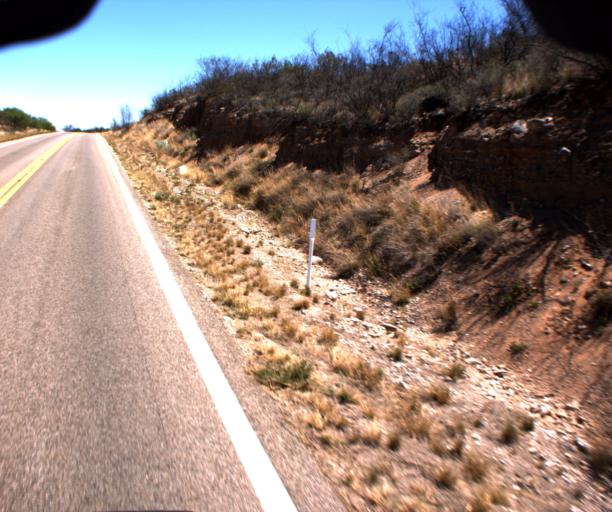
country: US
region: Arizona
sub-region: Cochise County
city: Tombstone
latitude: 31.7282
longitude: -110.1775
